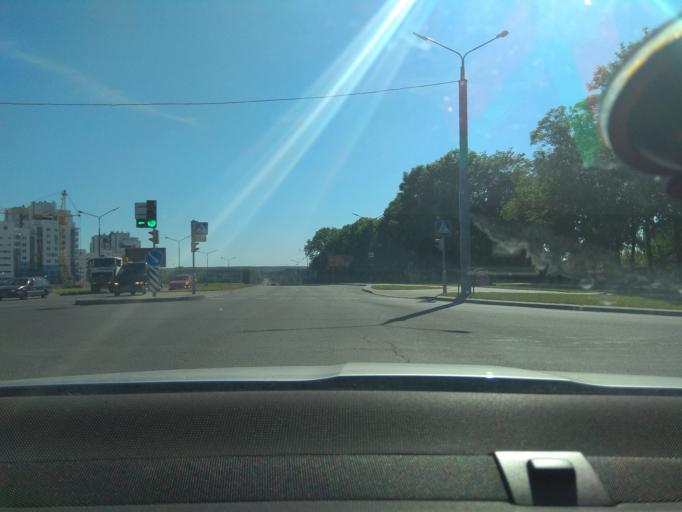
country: BY
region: Grodnenskaya
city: Hrodna
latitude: 53.6492
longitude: 23.7820
